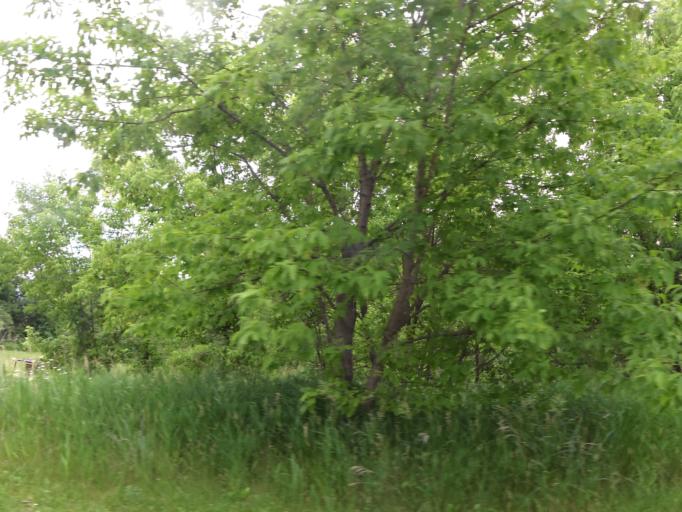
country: US
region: Minnesota
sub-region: Scott County
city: Prior Lake
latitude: 44.7555
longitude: -93.4545
